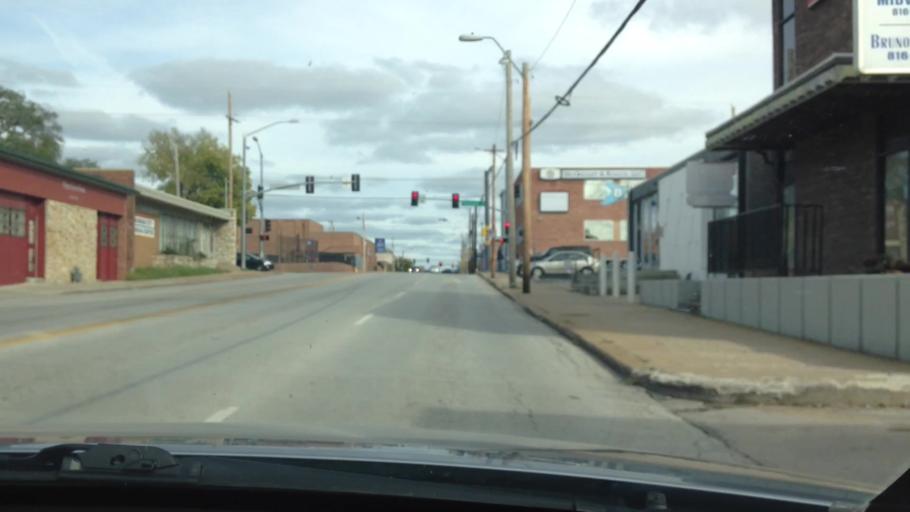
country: US
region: Kansas
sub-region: Johnson County
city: Westwood
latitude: 39.0568
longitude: -94.5939
